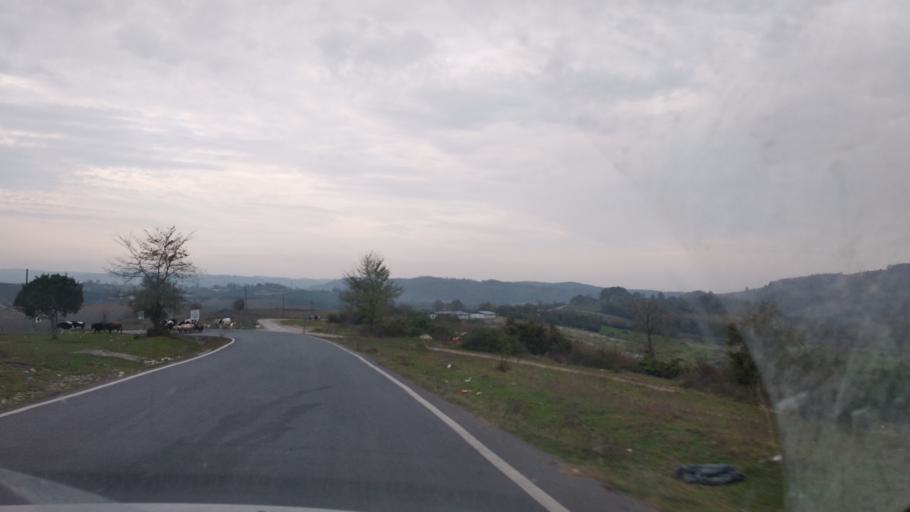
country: TR
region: Sakarya
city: Ortakoy
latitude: 41.0401
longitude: 30.6515
